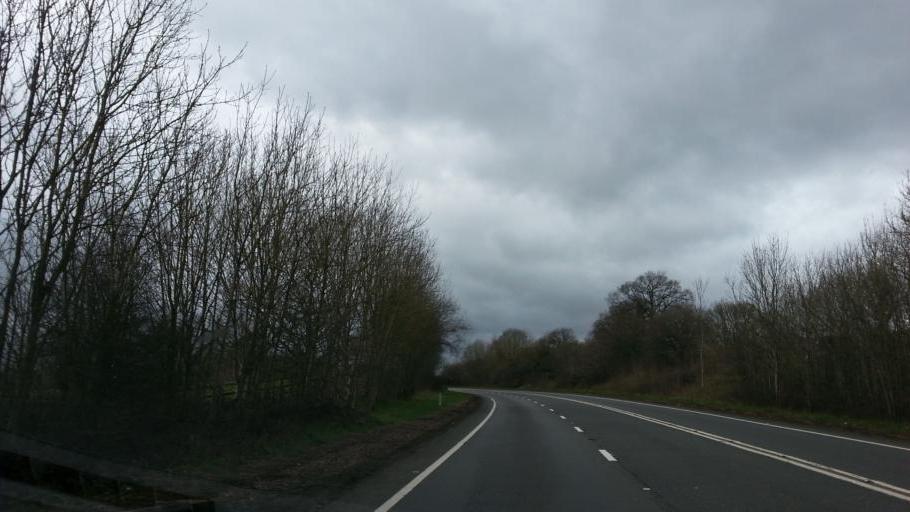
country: GB
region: England
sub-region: Devon
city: Tiverton
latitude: 50.9198
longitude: -3.5128
